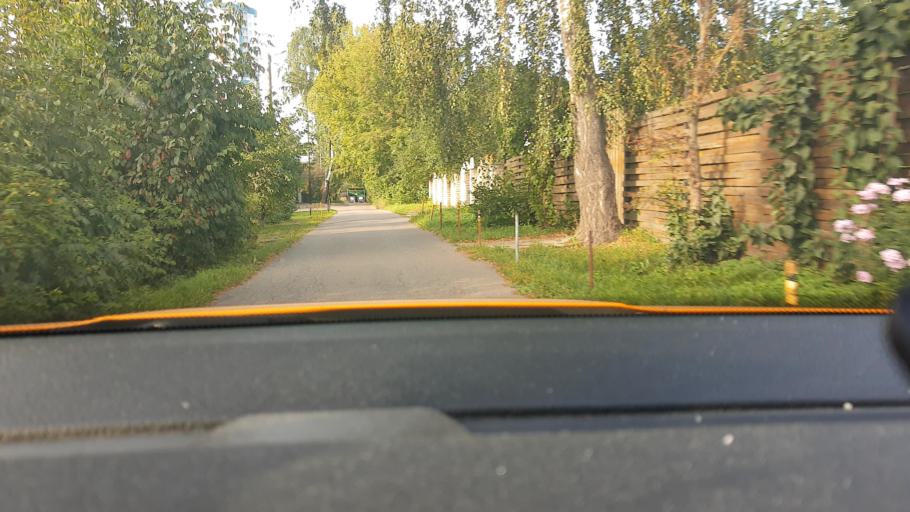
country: RU
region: Moskovskaya
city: Bolshevo
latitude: 55.9473
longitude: 37.8300
